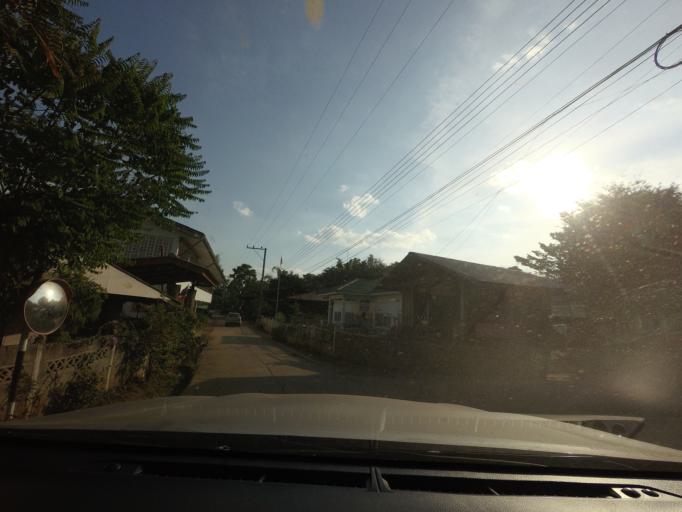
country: TH
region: Mae Hong Son
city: Wiang Nuea
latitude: 19.3975
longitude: 98.4043
